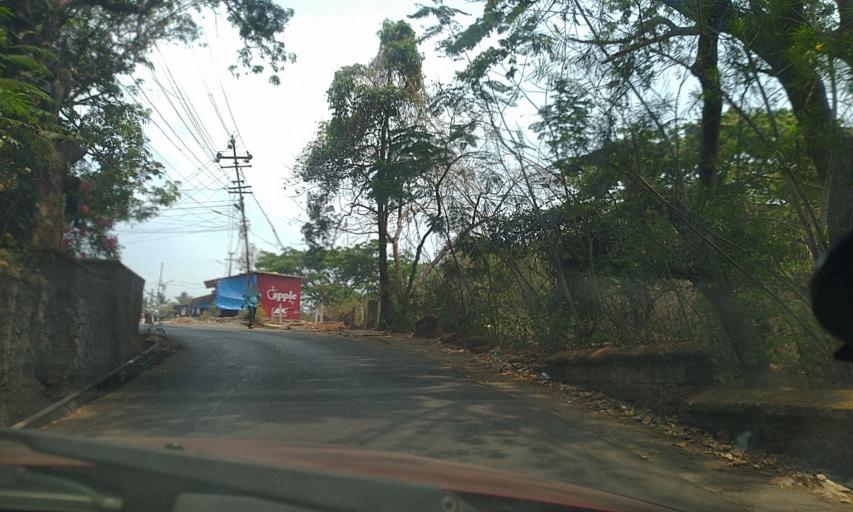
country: IN
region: Goa
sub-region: North Goa
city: Mapuca
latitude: 15.5962
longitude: 73.8100
